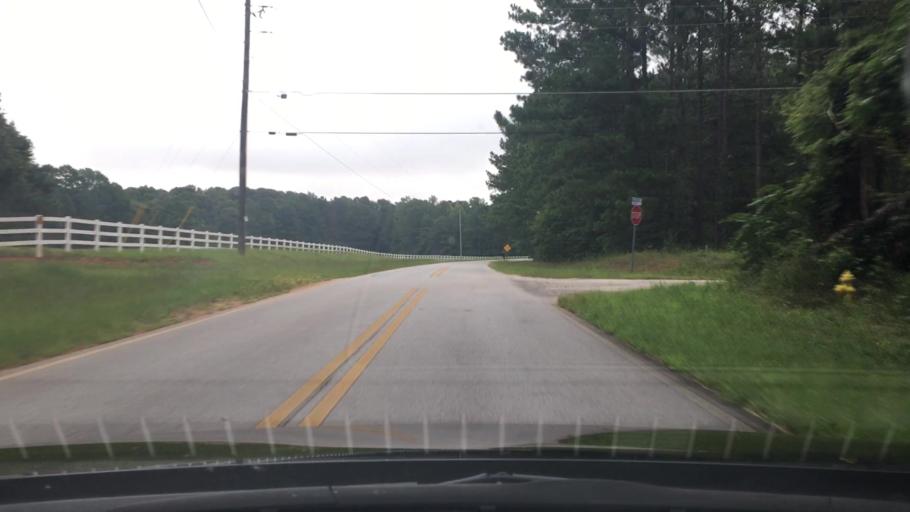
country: US
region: Georgia
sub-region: Spalding County
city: Experiment
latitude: 33.2818
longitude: -84.4030
